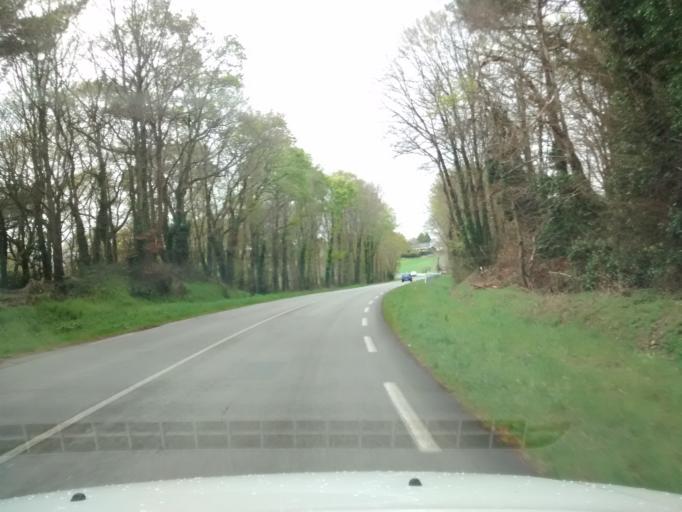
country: FR
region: Brittany
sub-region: Departement du Morbihan
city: Gestel
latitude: 47.7925
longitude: -3.4606
